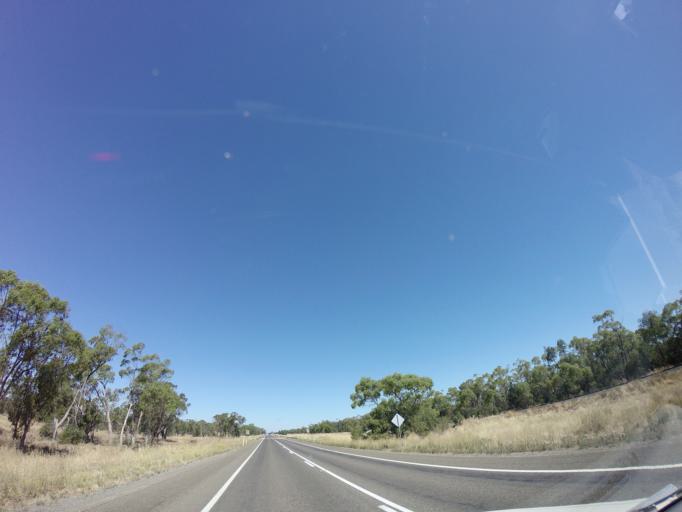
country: AU
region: New South Wales
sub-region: Bogan
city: Nyngan
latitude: -31.5703
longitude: 147.2122
